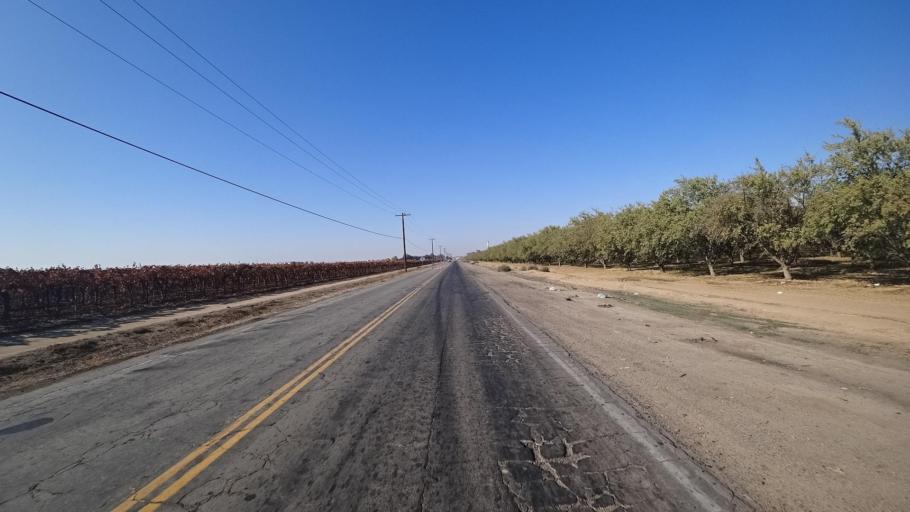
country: US
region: California
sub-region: Kern County
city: McFarland
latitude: 35.7180
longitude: -119.2241
